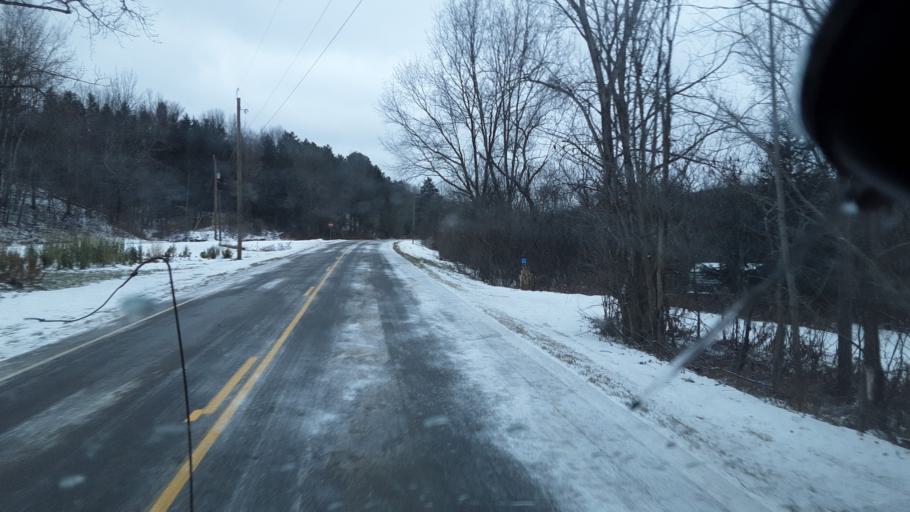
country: US
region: New York
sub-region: Allegany County
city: Friendship
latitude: 42.2758
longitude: -78.1314
